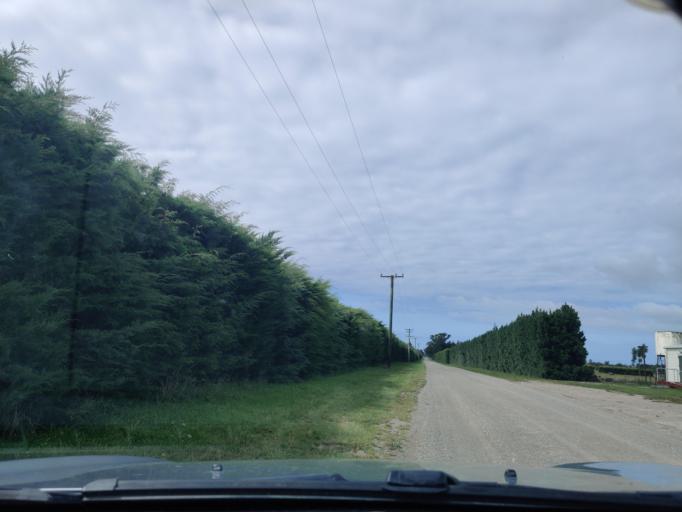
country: NZ
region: Canterbury
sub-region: Hurunui District
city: Amberley
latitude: -43.2095
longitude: 172.6969
